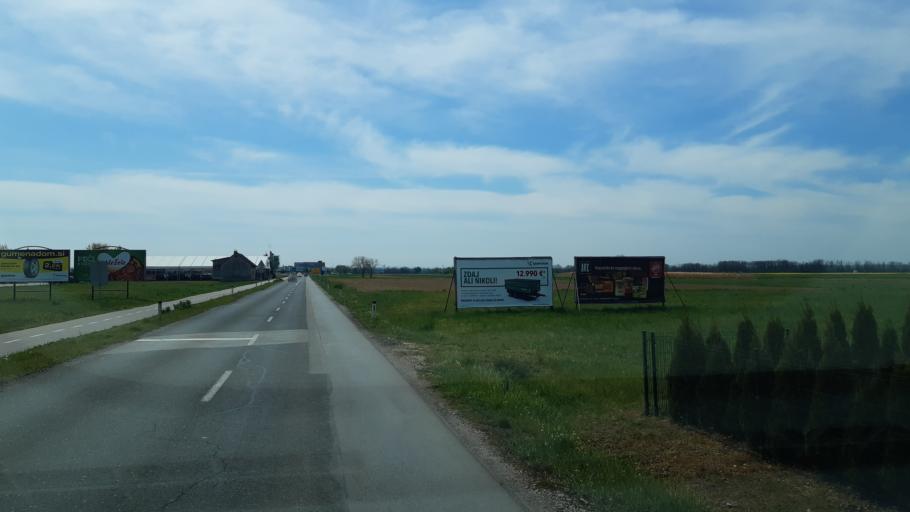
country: SI
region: Murska Sobota
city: Murska Sobota
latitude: 46.6526
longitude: 16.1693
